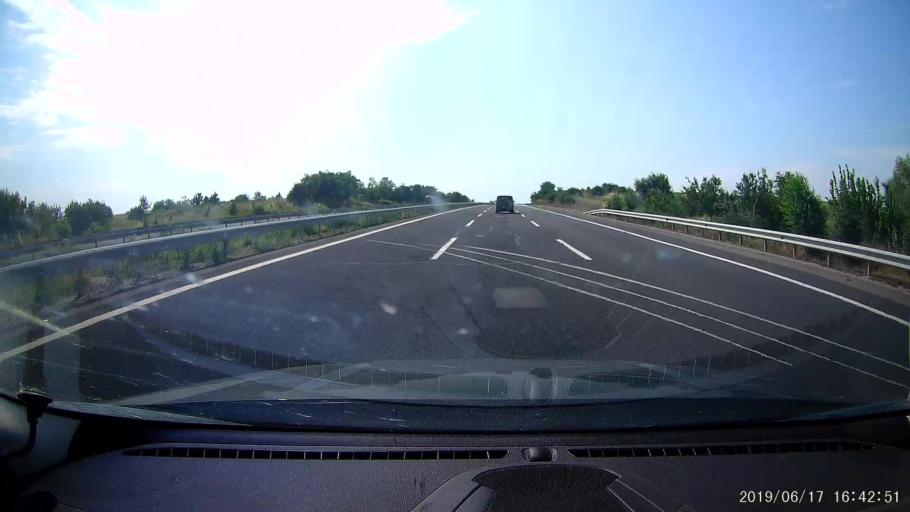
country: TR
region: Kirklareli
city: Luleburgaz
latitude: 41.4760
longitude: 27.3109
